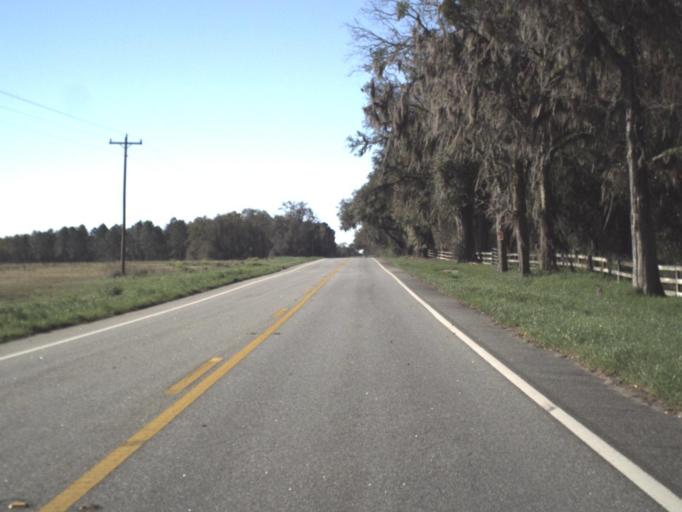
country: US
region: Georgia
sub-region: Brooks County
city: Quitman
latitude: 30.6386
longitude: -83.6445
